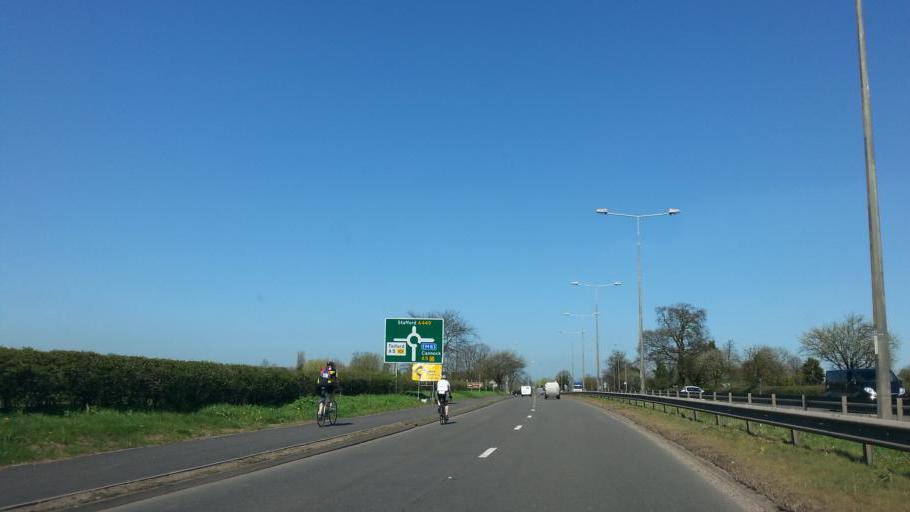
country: GB
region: England
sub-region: Staffordshire
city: Penkridge
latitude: 52.6908
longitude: -2.1317
